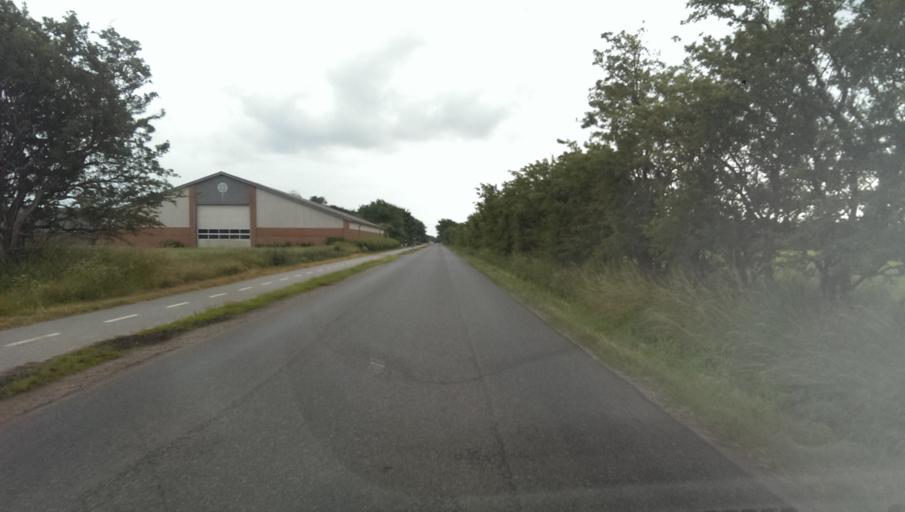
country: DK
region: South Denmark
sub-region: Esbjerg Kommune
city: Bramming
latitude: 55.4457
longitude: 8.7229
